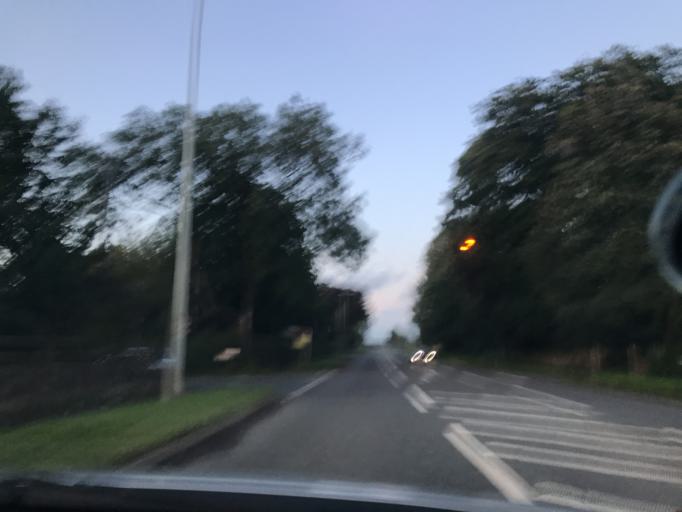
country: GB
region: England
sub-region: Cheshire West and Chester
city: Tarvin
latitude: 53.2010
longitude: -2.7612
